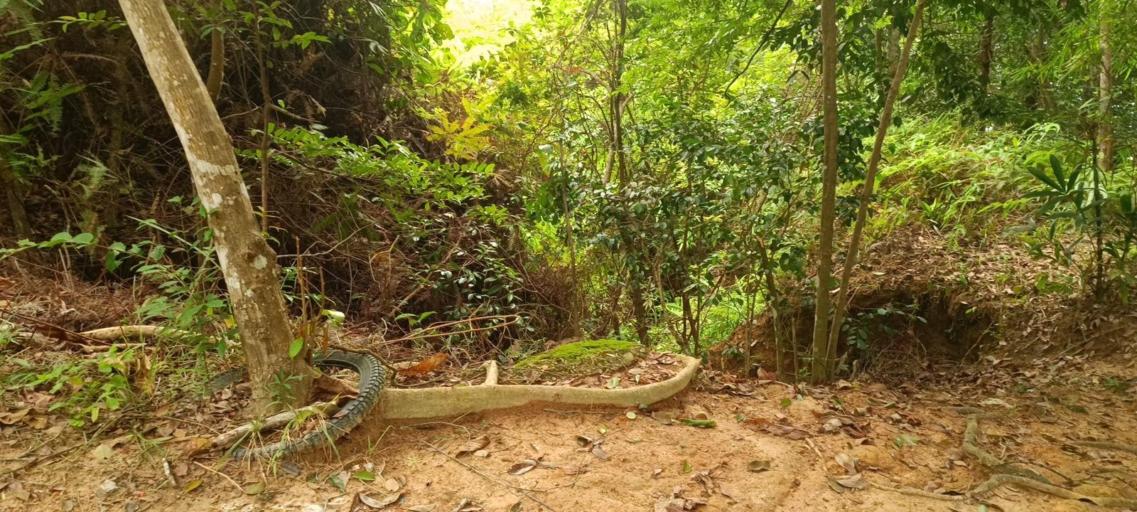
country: MY
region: Penang
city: Tanjung Tokong
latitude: 5.4305
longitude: 100.2927
